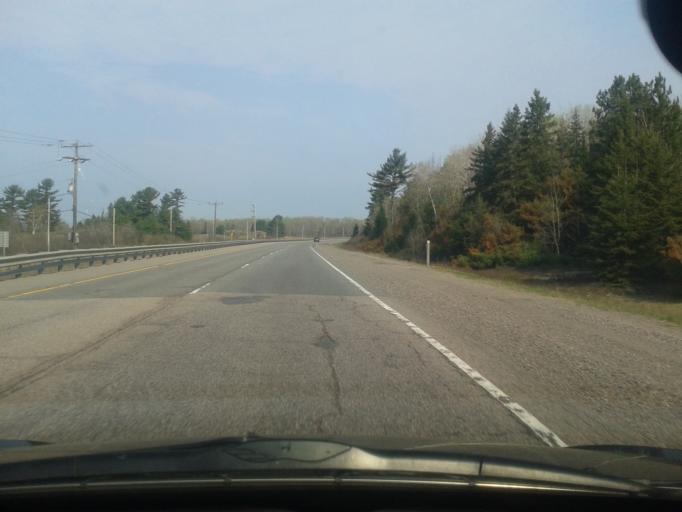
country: CA
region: Ontario
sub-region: Nipissing District
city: North Bay
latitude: 46.2875
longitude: -79.4153
